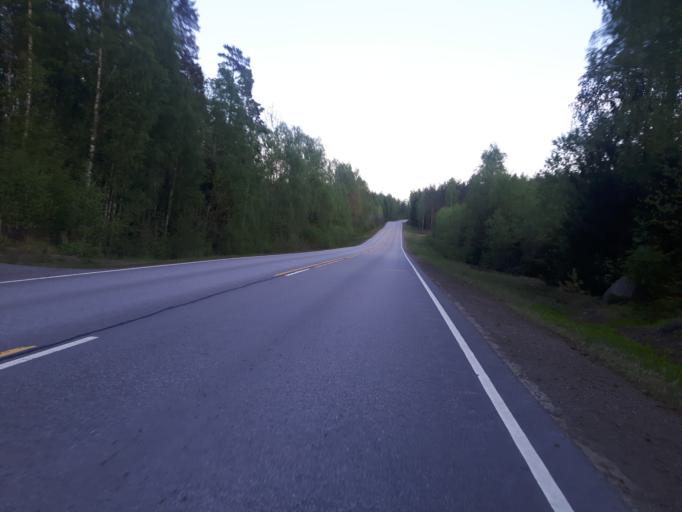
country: FI
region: Uusimaa
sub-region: Loviisa
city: Perna
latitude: 60.4590
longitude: 26.0720
